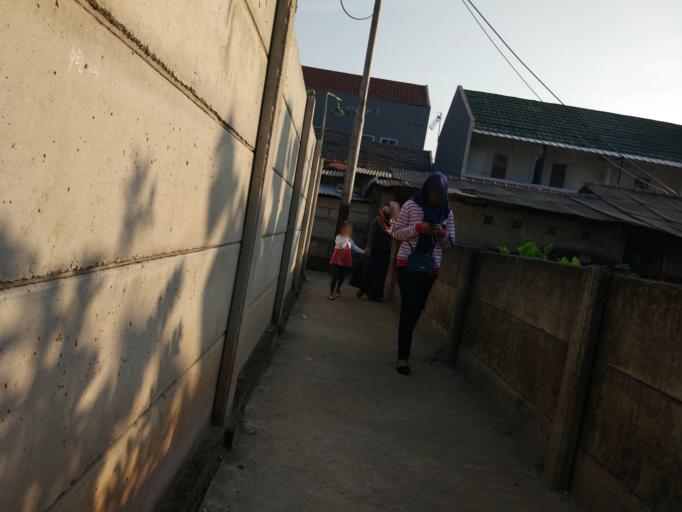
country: ID
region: Jakarta Raya
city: Jakarta
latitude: -6.2422
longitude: 106.8590
